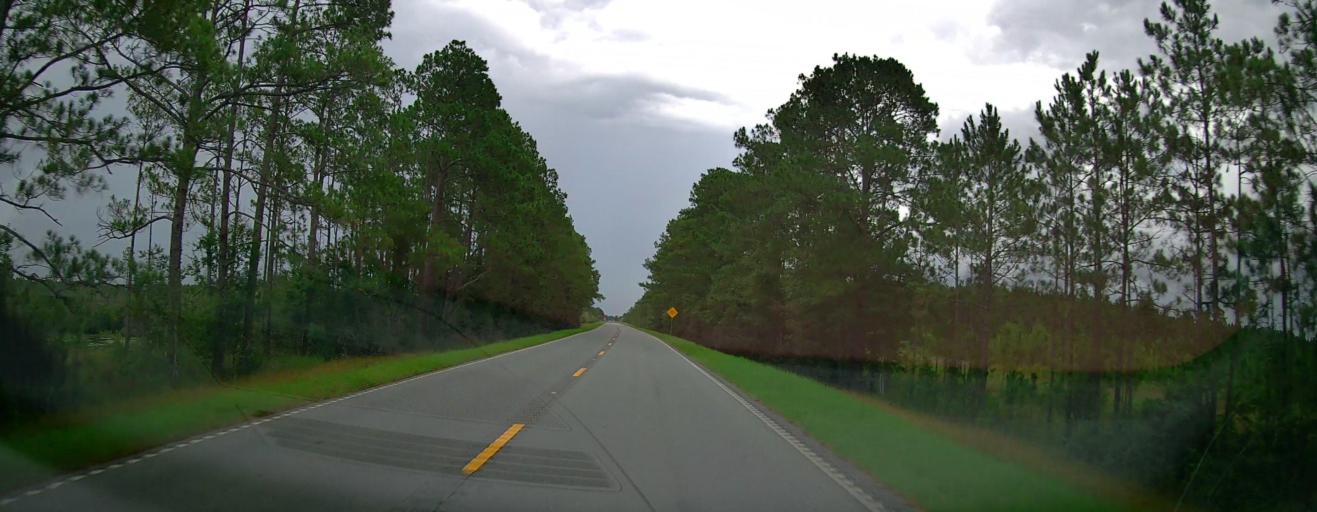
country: US
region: Georgia
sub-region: Brantley County
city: Nahunta
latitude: 31.3559
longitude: -82.0549
